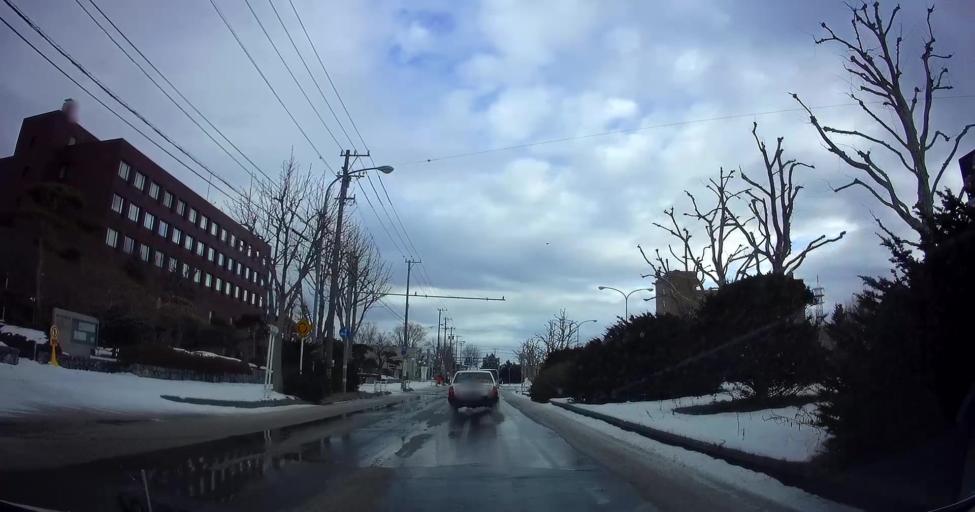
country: JP
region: Hokkaido
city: Hakodate
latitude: 41.7784
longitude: 140.7378
